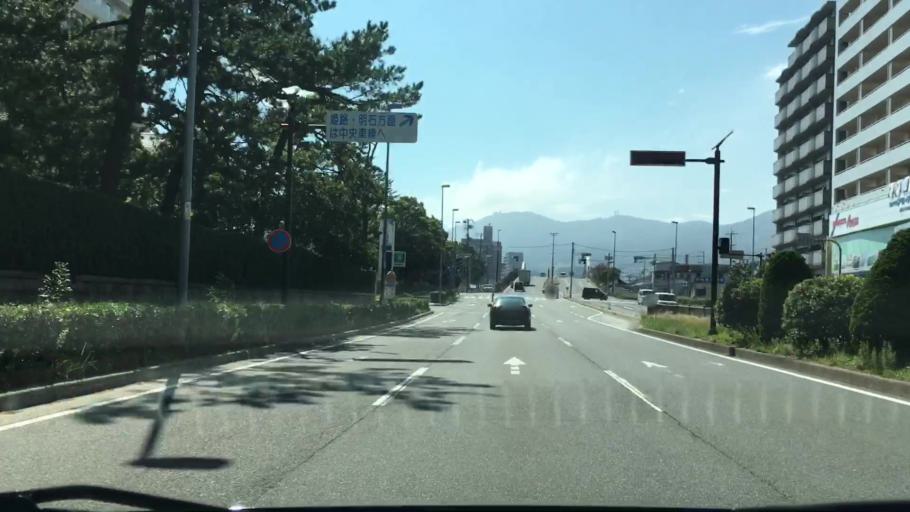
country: JP
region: Hyogo
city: Kobe
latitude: 34.6442
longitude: 135.1235
